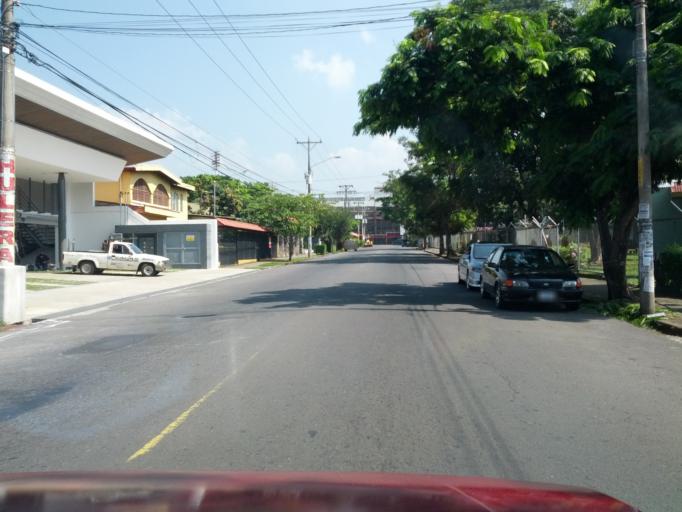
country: CR
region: Alajuela
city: Alajuela
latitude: 10.0212
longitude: -84.2115
